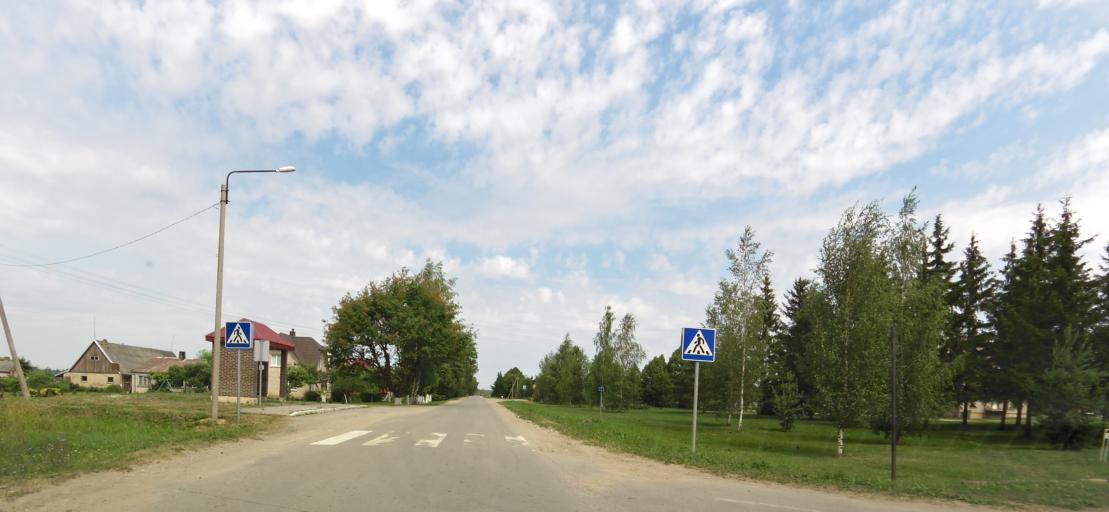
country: LT
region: Panevezys
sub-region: Birzai
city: Birzai
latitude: 56.2634
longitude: 24.6091
